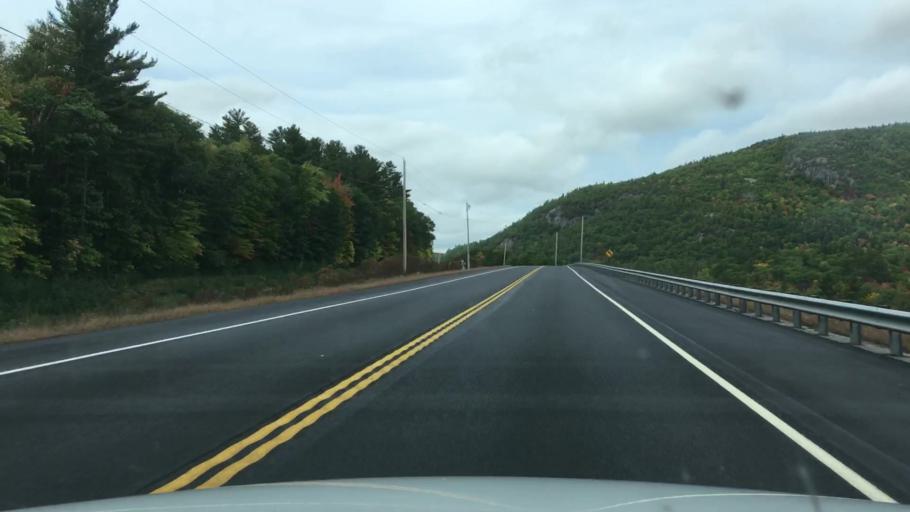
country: US
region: Maine
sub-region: Oxford County
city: Bethel
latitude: 44.4050
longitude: -70.9192
